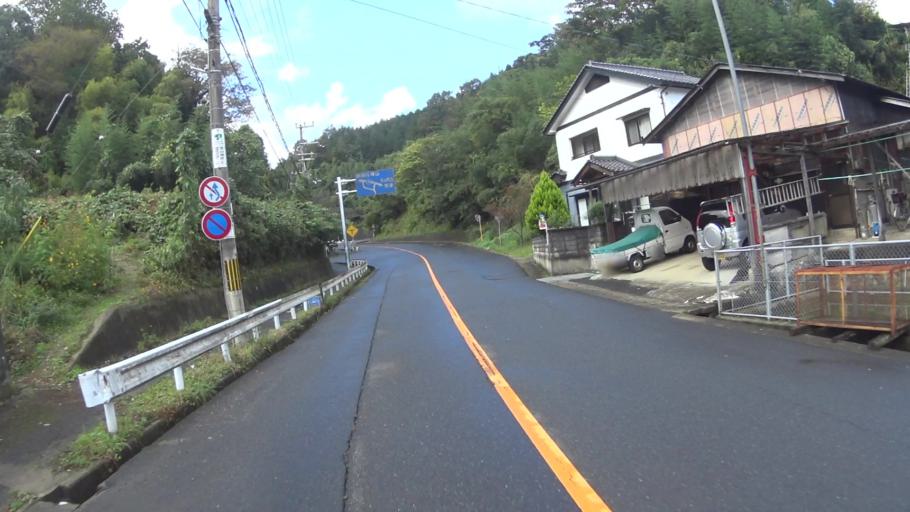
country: JP
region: Kyoto
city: Miyazu
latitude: 35.5521
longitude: 135.1480
